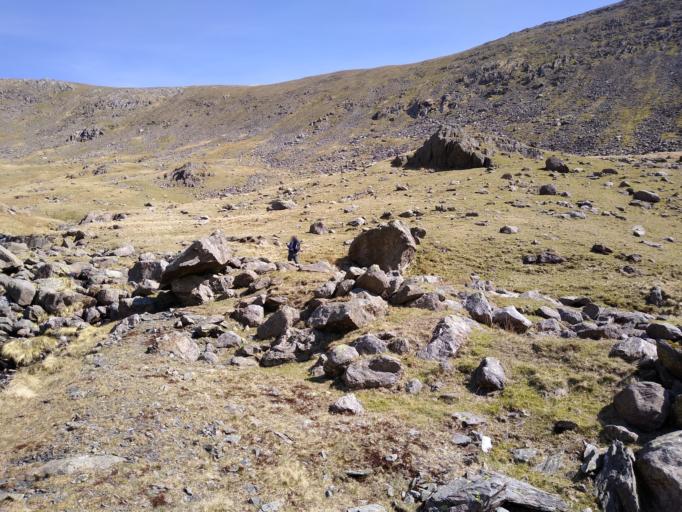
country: GB
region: England
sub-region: Cumbria
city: Ambleside
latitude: 54.3845
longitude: -3.1331
